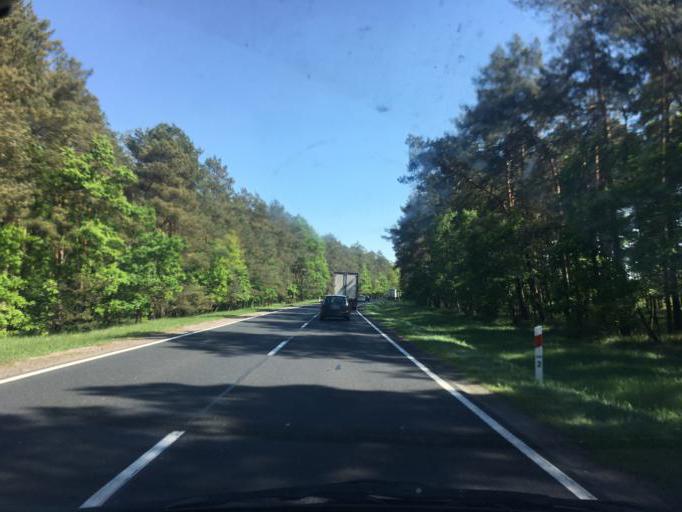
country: PL
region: Kujawsko-Pomorskie
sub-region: Powiat torunski
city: Wielka Nieszawka
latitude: 53.0289
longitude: 18.4141
